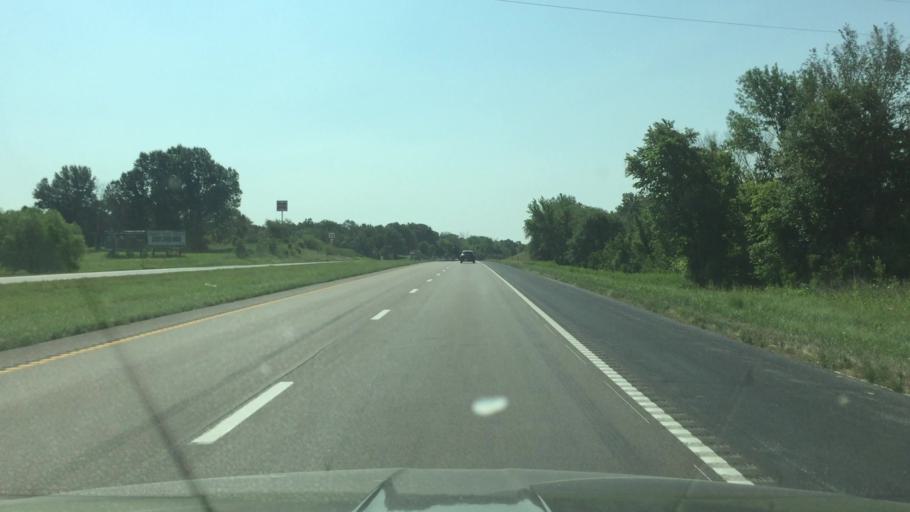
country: US
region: Missouri
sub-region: Pettis County
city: Sedalia
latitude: 38.7368
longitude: -93.3154
